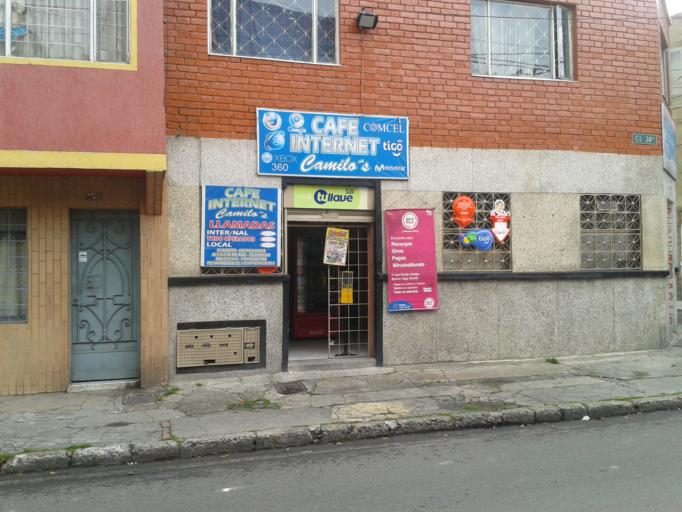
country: CO
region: Bogota D.C.
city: Bogota
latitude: 4.5849
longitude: -74.1068
